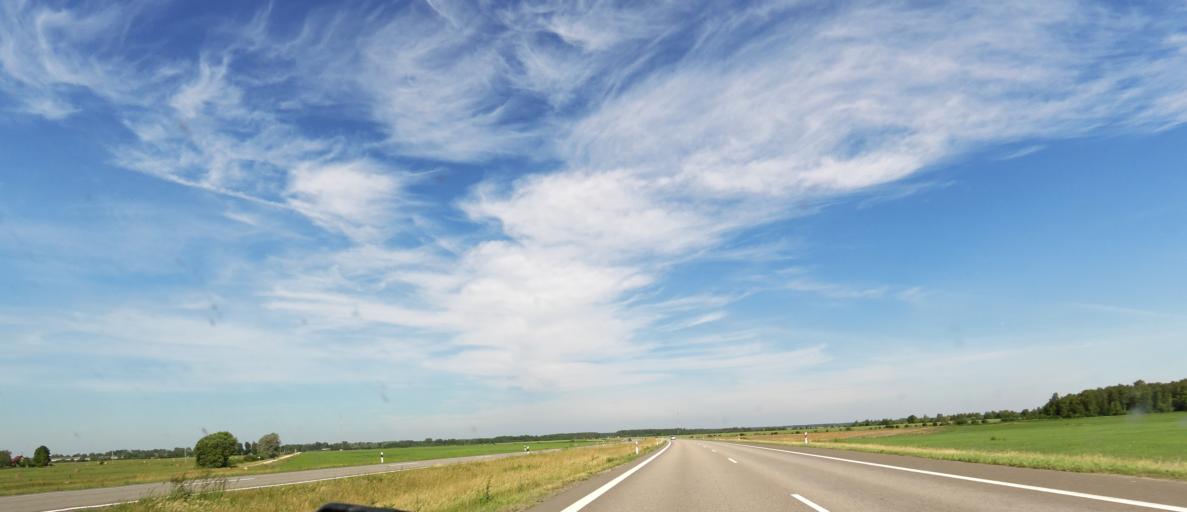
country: LT
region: Panevezys
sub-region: Panevezys City
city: Panevezys
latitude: 55.6012
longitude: 24.4417
